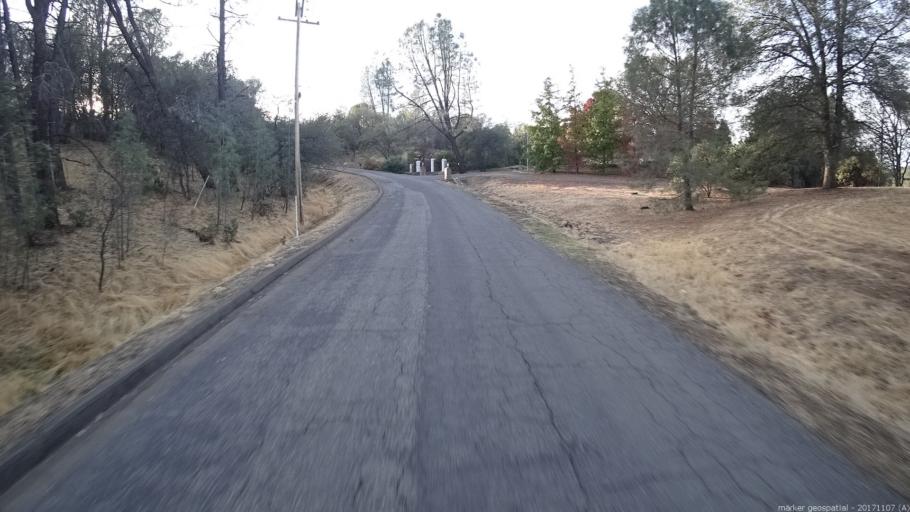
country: US
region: California
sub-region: Shasta County
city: Shasta
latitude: 40.5390
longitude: -122.4830
